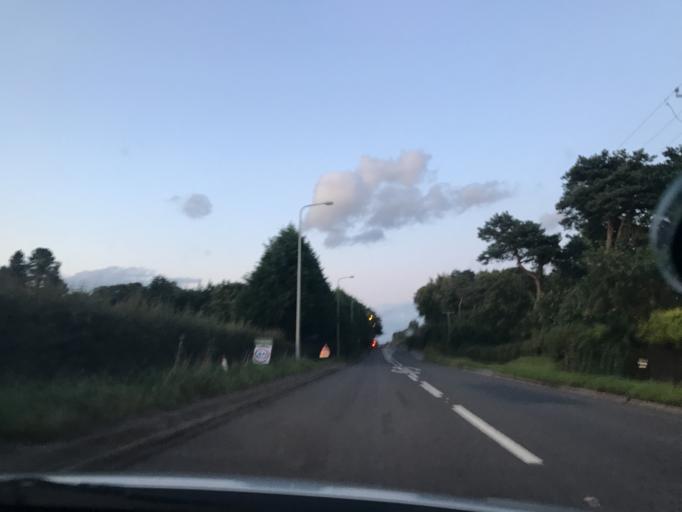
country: GB
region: England
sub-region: Cheshire West and Chester
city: Oakmere
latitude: 53.2167
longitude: -2.6454
